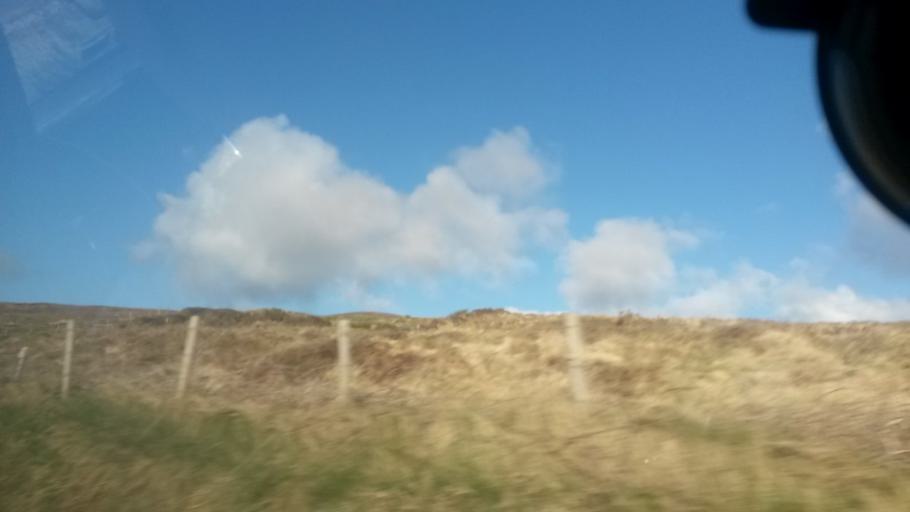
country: IE
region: Munster
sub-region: Ciarrai
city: Dingle
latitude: 52.1403
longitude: -10.4636
